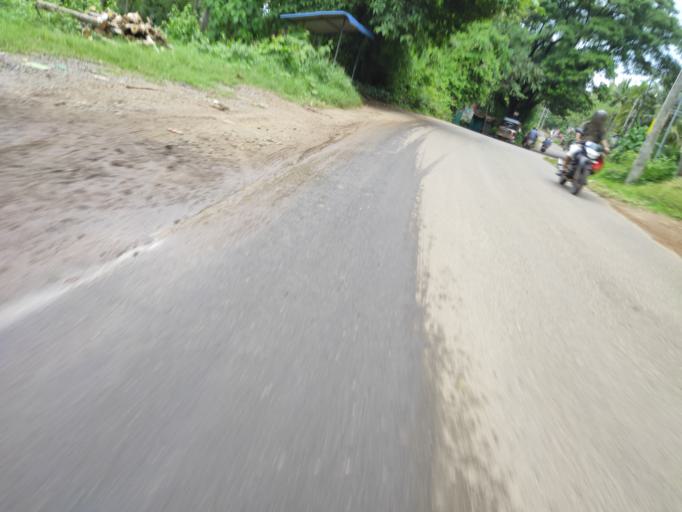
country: IN
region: Kerala
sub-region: Malappuram
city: Manjeri
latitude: 11.1914
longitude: 76.2541
